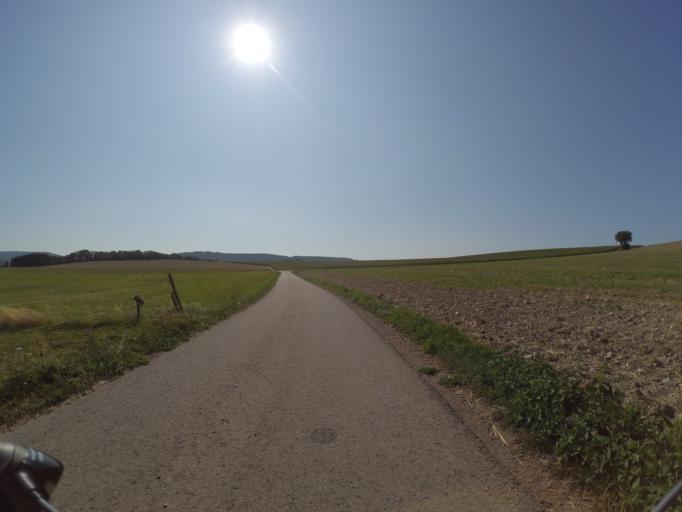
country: DE
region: Rheinland-Pfalz
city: Deuselbach
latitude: 49.7567
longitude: 7.0439
